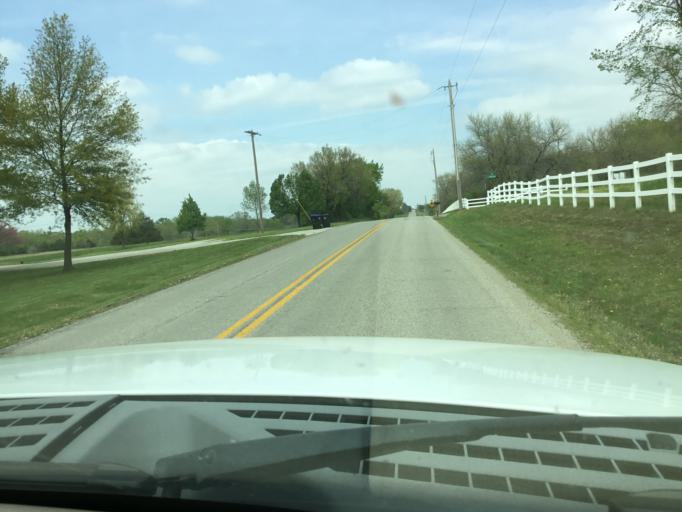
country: US
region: Kansas
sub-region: Shawnee County
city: Topeka
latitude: 38.9688
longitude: -95.6142
